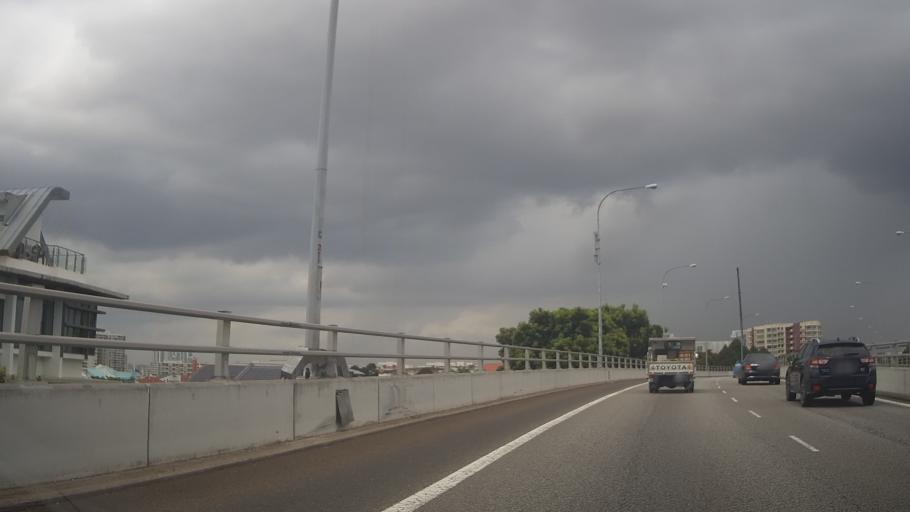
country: SG
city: Singapore
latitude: 1.3437
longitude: 103.8706
